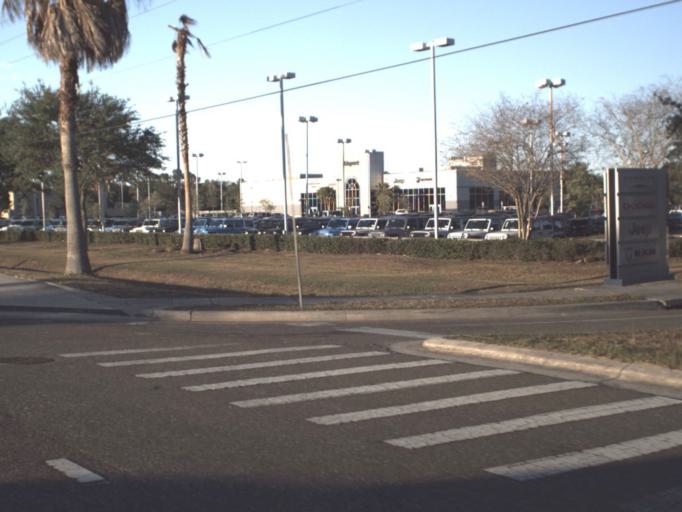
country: US
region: Florida
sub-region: Orange County
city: Conway
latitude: 28.4718
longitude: -81.3099
